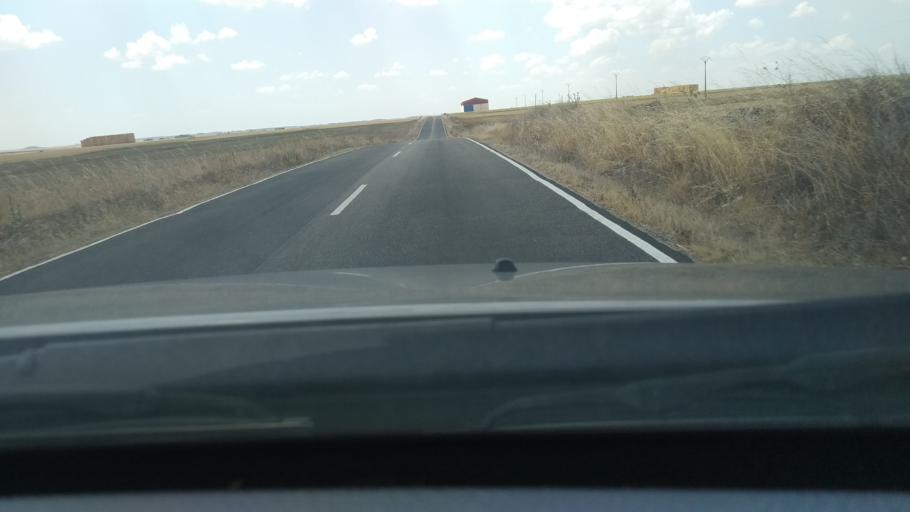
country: ES
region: Castille and Leon
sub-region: Provincia de Burgos
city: Villafruela
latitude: 41.9328
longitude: -3.8840
